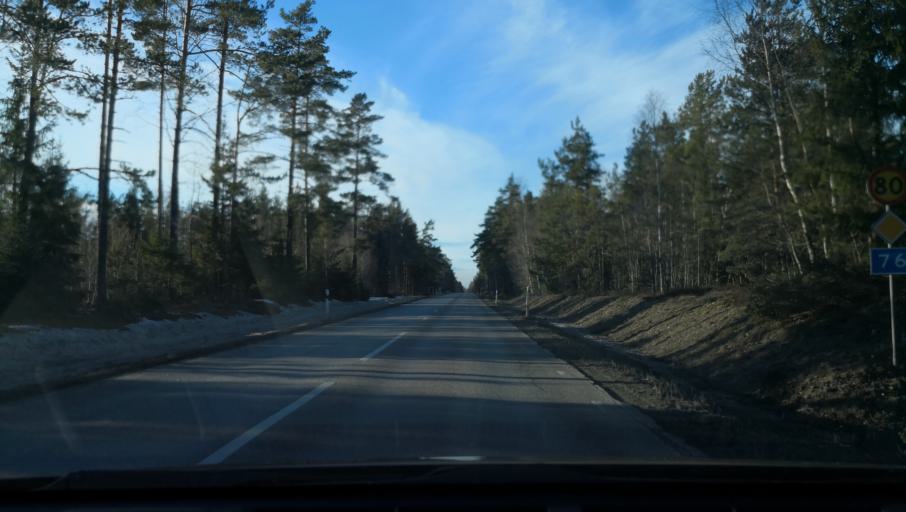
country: SE
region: Uppsala
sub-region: Osthammars Kommun
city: OEsthammar
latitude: 60.2668
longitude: 18.3313
